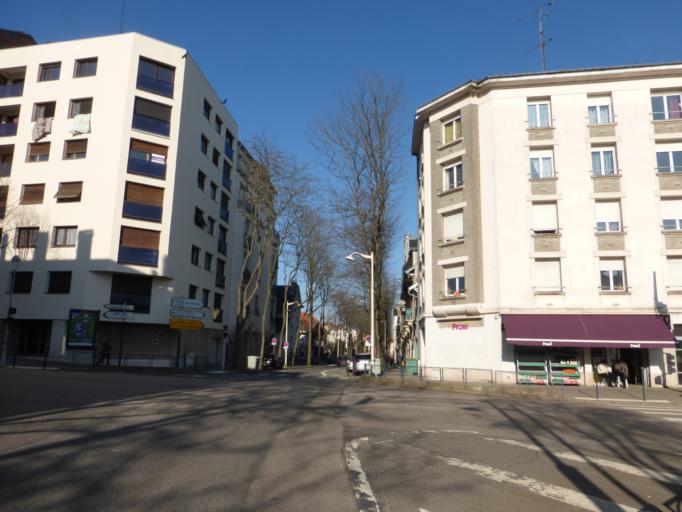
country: FR
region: Lorraine
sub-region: Departement de Meurthe-et-Moselle
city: Nancy
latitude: 48.6756
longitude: 6.1819
